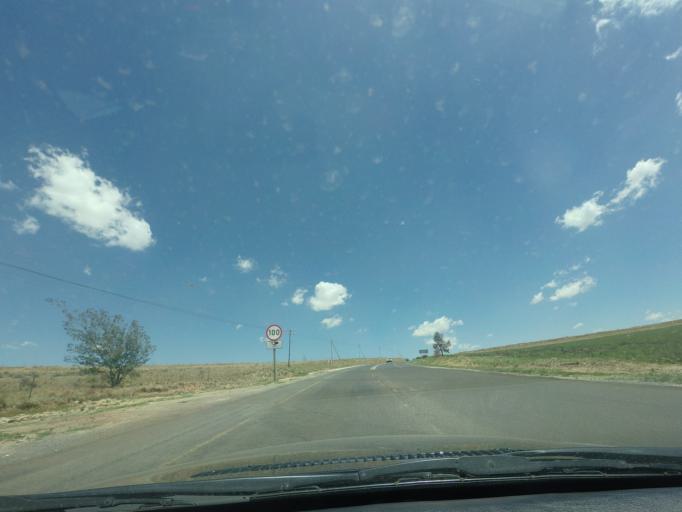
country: ZA
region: Orange Free State
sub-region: Thabo Mofutsanyana District Municipality
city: Ladybrand
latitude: -29.2129
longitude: 27.4506
